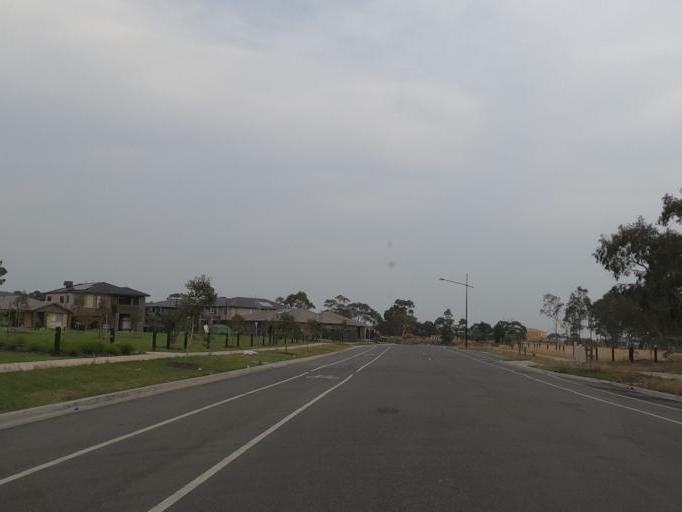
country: AU
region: Victoria
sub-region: Hume
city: Greenvale
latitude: -37.6290
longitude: 144.8781
